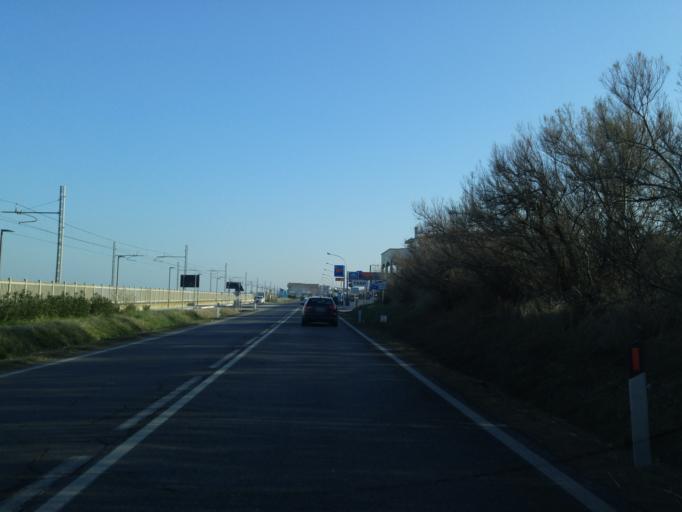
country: IT
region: The Marches
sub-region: Provincia di Pesaro e Urbino
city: Fenile
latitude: 43.8635
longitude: 12.9885
